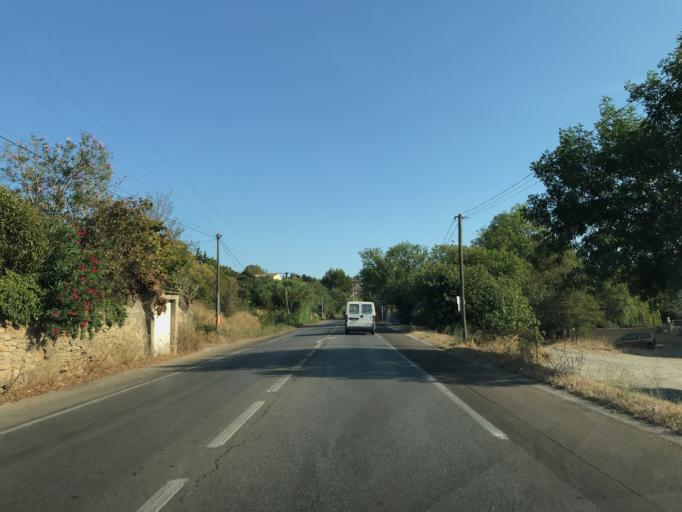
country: FR
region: Provence-Alpes-Cote d'Azur
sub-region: Departement des Bouches-du-Rhone
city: Saint-Chamas
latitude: 43.5601
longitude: 5.0307
